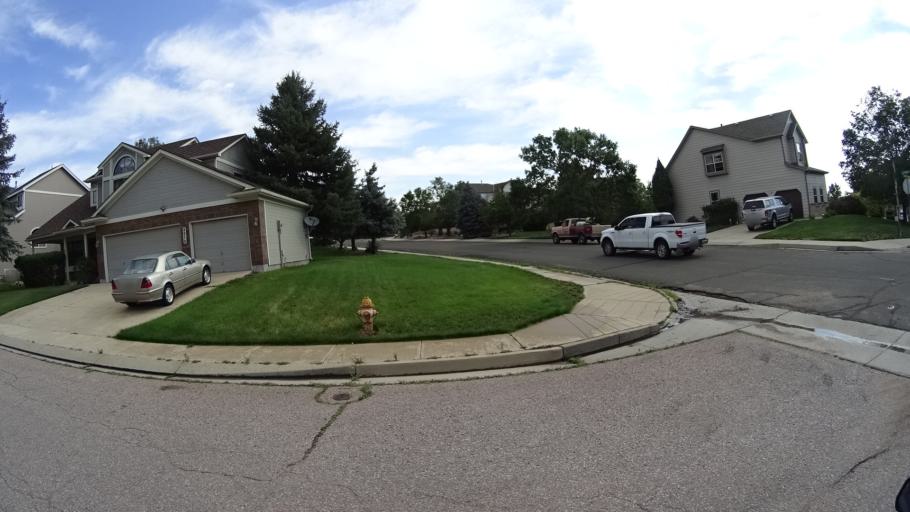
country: US
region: Colorado
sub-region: El Paso County
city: Air Force Academy
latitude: 38.9505
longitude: -104.8612
